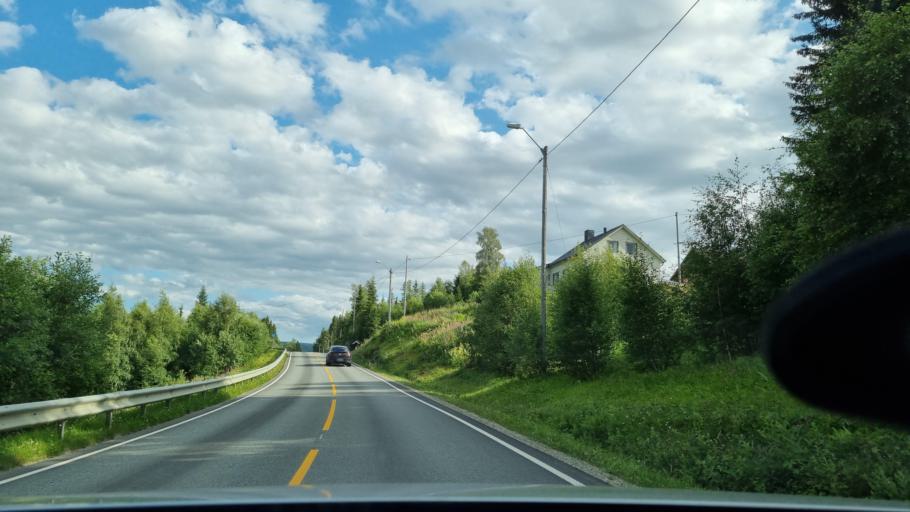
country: NO
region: Sor-Trondelag
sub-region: Holtalen
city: Alen
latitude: 62.8243
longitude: 11.3273
